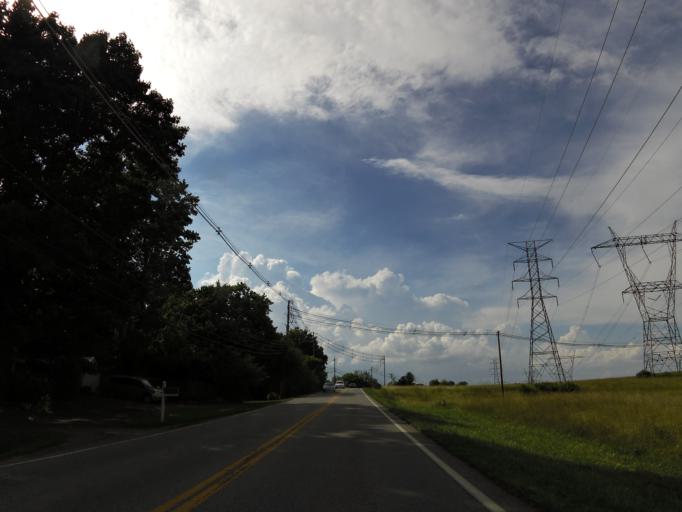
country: US
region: Tennessee
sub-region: Blount County
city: Alcoa
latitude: 35.7892
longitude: -84.0106
